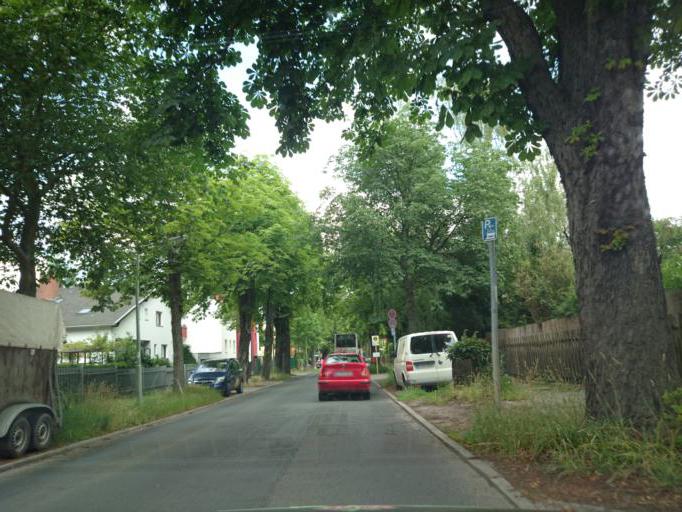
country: DE
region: Berlin
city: Marienfelde
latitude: 52.4194
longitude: 13.3514
